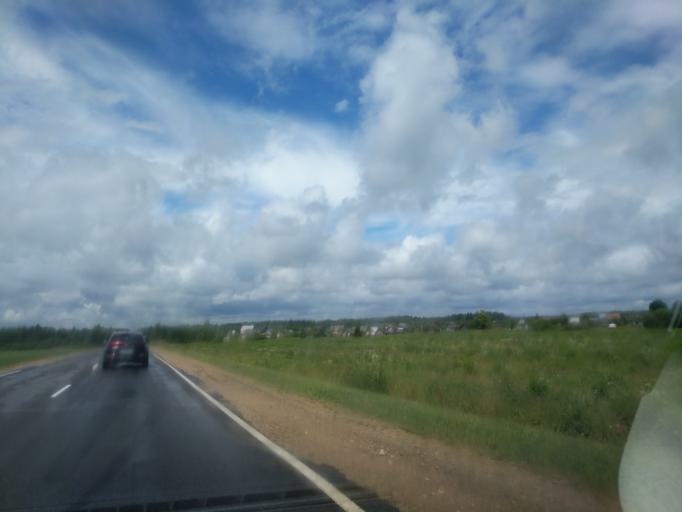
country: BY
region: Minsk
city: Il'ya
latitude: 54.3947
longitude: 27.3409
